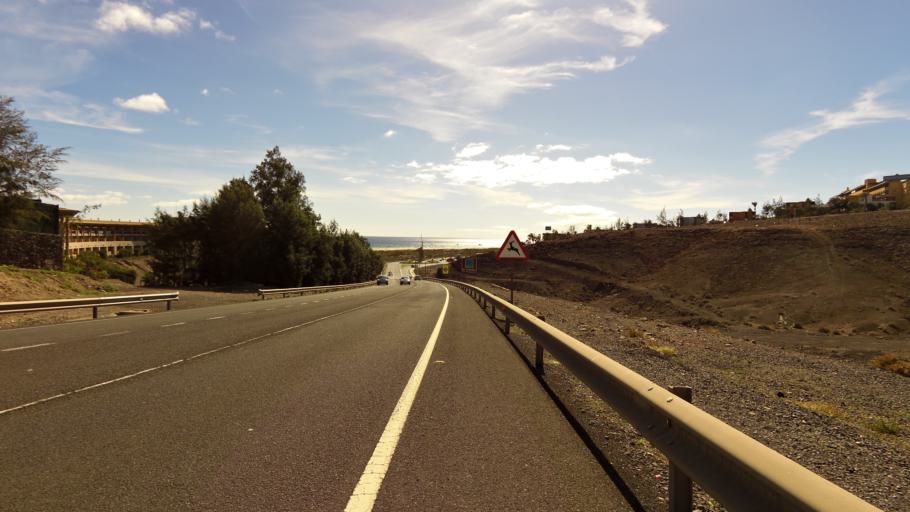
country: ES
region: Canary Islands
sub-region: Provincia de Las Palmas
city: Pajara
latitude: 28.0572
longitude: -14.3215
